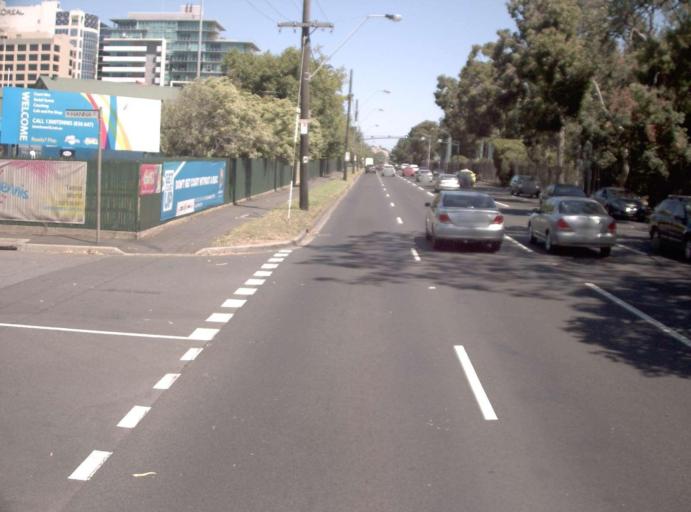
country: AU
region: Victoria
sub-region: Port Phillip
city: South Melbourne
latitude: -37.8444
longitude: 144.9762
